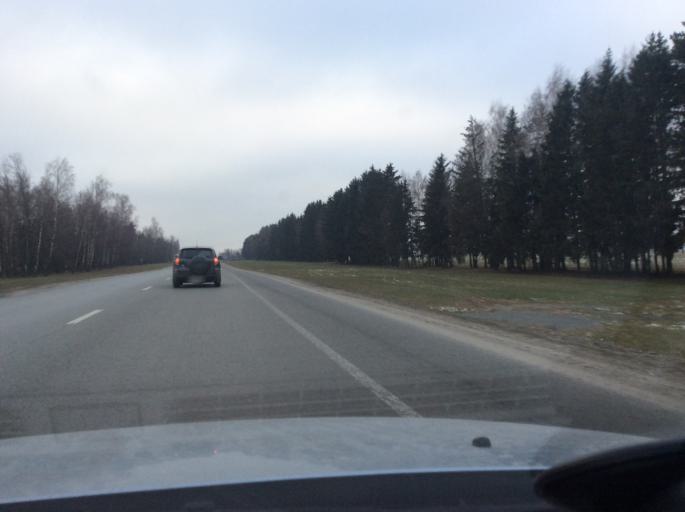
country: RU
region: Moskovskaya
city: Troitsk
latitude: 55.3641
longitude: 37.1974
